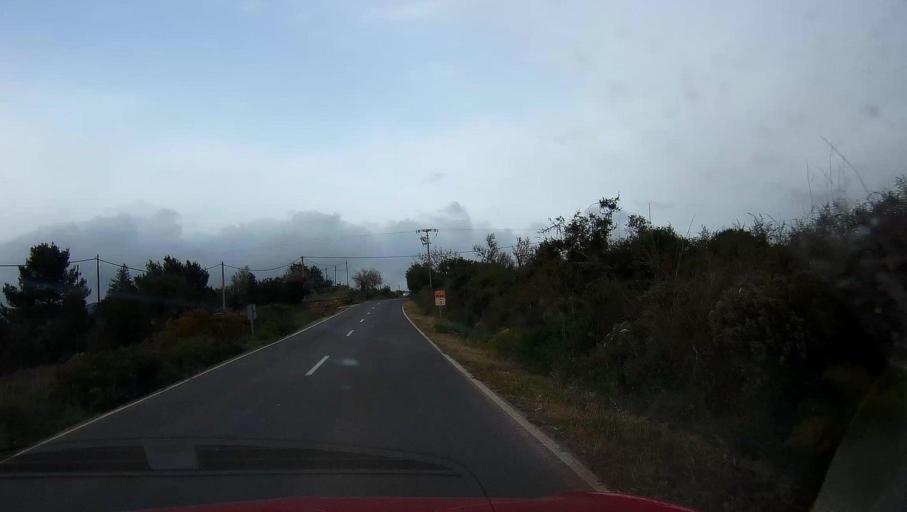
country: ES
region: Balearic Islands
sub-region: Illes Balears
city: Sant Joan de Labritja
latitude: 39.0596
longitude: 1.4665
